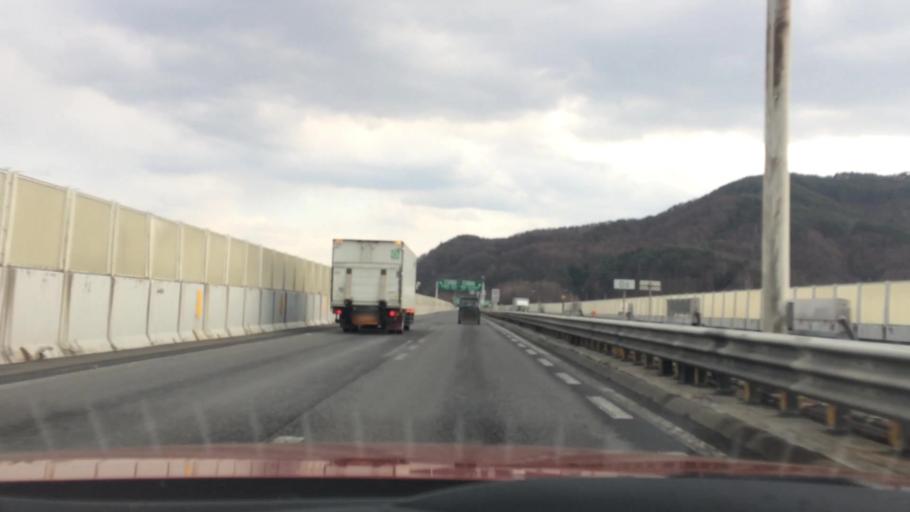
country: JP
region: Nagano
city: Okaya
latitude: 36.0567
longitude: 138.0400
